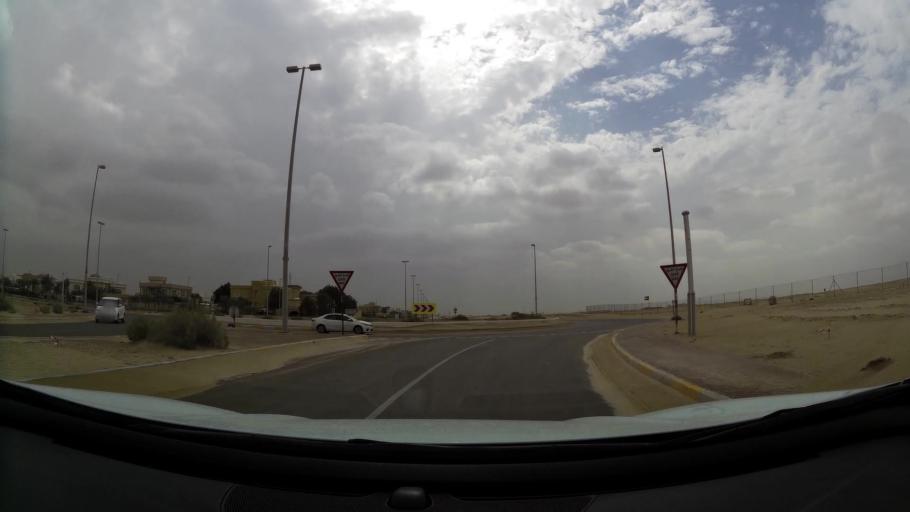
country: AE
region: Abu Dhabi
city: Abu Dhabi
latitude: 24.3897
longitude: 54.6408
